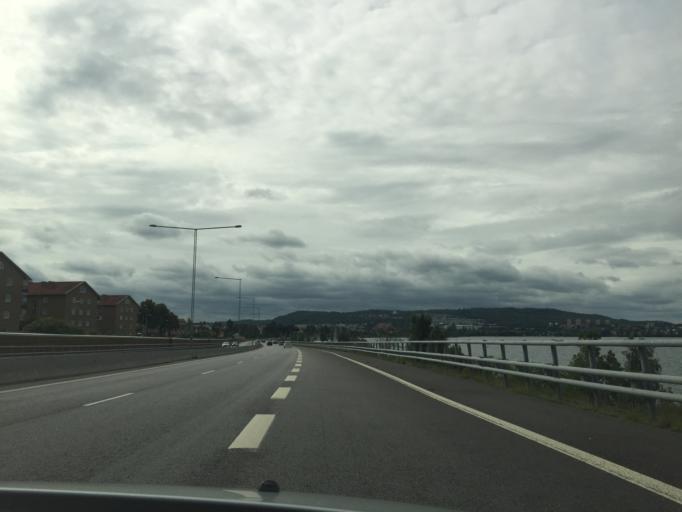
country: SE
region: Joenkoeping
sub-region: Jonkopings Kommun
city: Huskvarna
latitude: 57.8099
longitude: 14.2713
